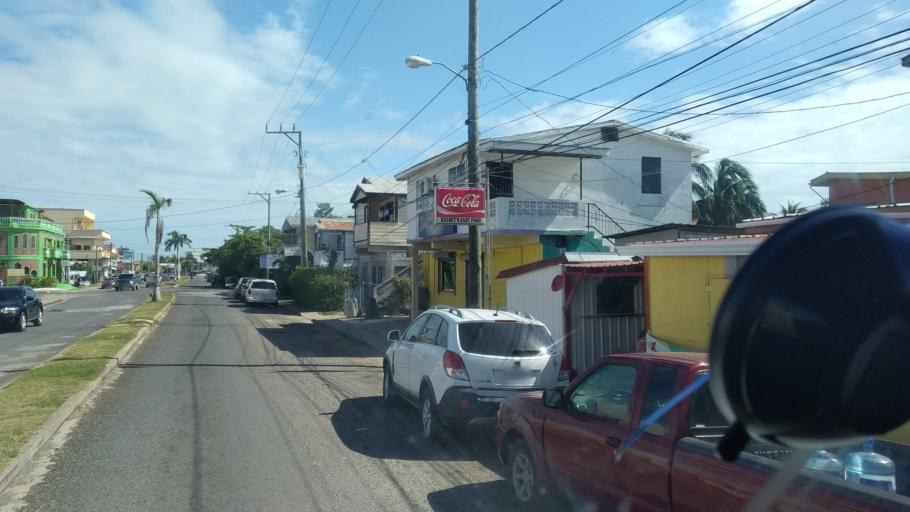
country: BZ
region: Belize
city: Belize City
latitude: 17.5068
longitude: -88.1944
